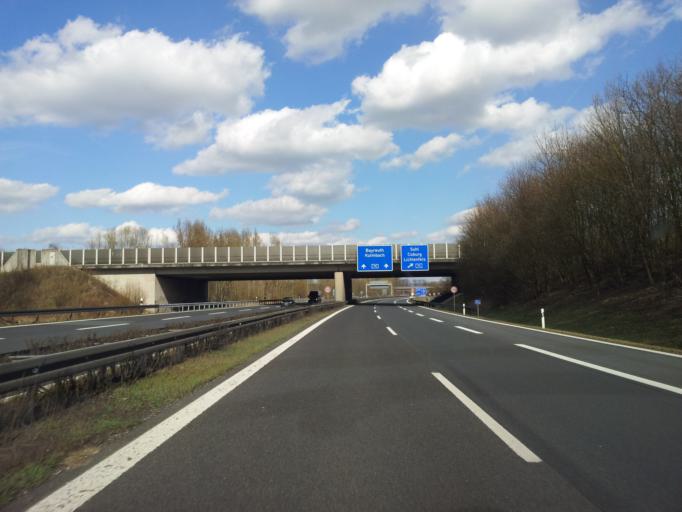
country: DE
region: Bavaria
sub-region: Upper Franconia
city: Gundelsheim
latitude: 49.9284
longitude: 10.9156
